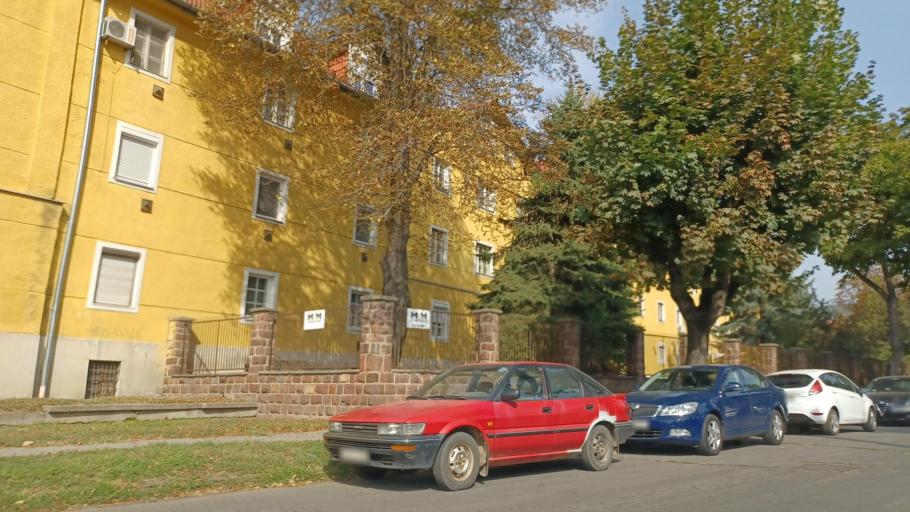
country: HU
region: Baranya
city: Pecs
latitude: 46.0663
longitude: 18.2182
